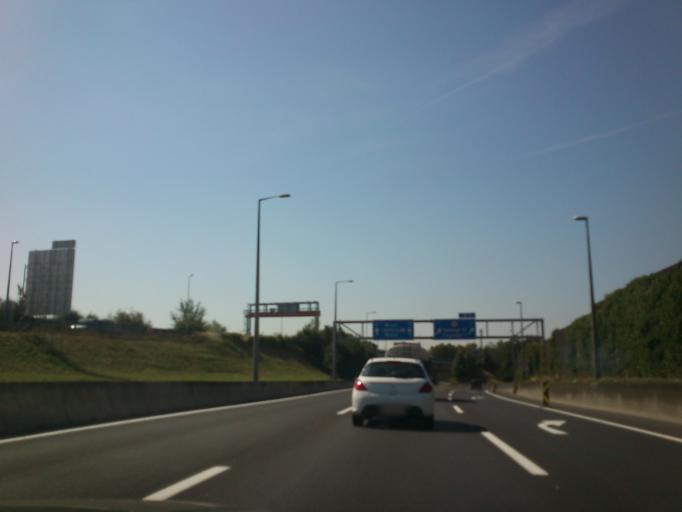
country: AT
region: Upper Austria
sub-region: Linz Stadt
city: Linz
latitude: 48.2640
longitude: 14.2972
